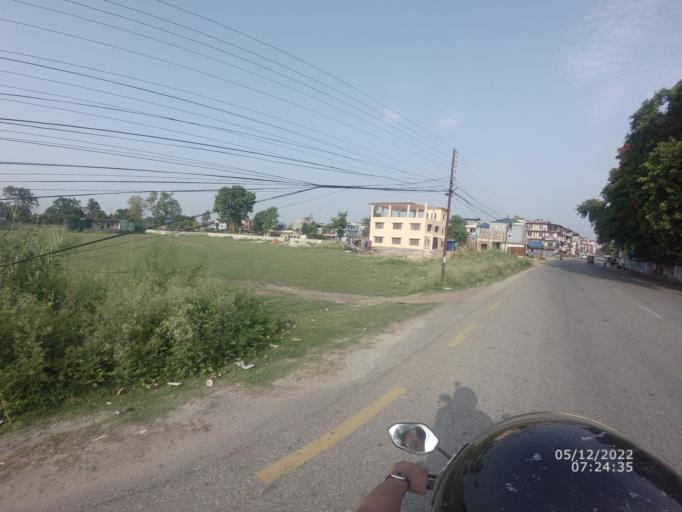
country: NP
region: Central Region
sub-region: Narayani Zone
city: Bharatpur
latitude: 27.6804
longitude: 84.4355
